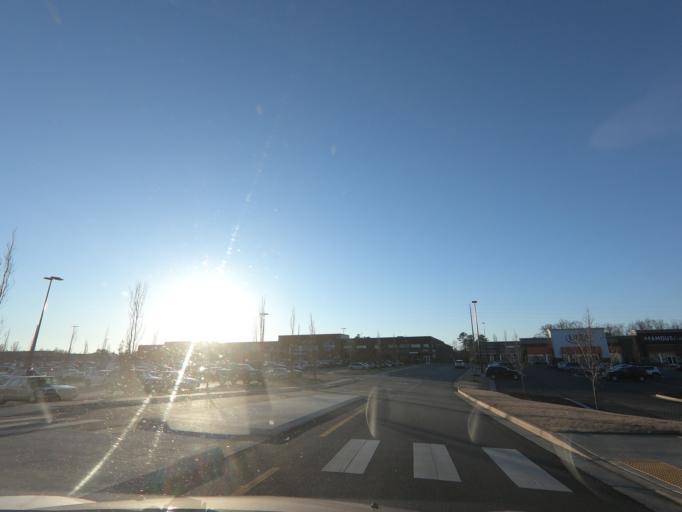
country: US
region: Georgia
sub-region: Dawson County
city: Dawsonville
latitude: 34.3504
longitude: -84.0514
